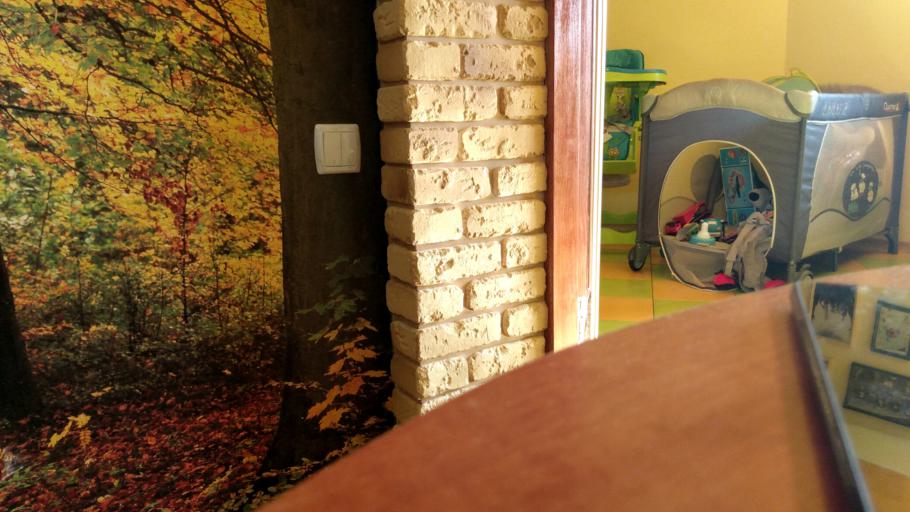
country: RU
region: Tverskaya
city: Gorodnya
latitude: 56.7390
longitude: 36.3501
